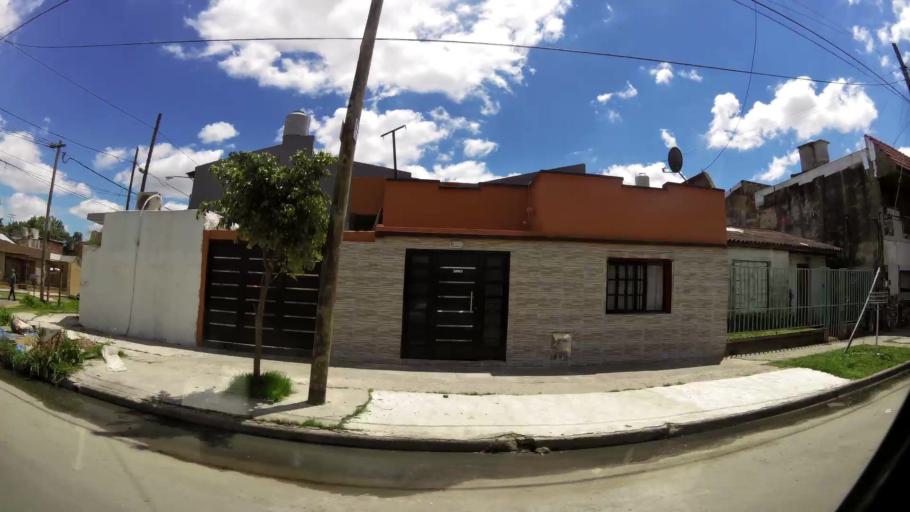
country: AR
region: Buenos Aires
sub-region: Partido de Lanus
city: Lanus
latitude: -34.7046
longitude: -58.4244
